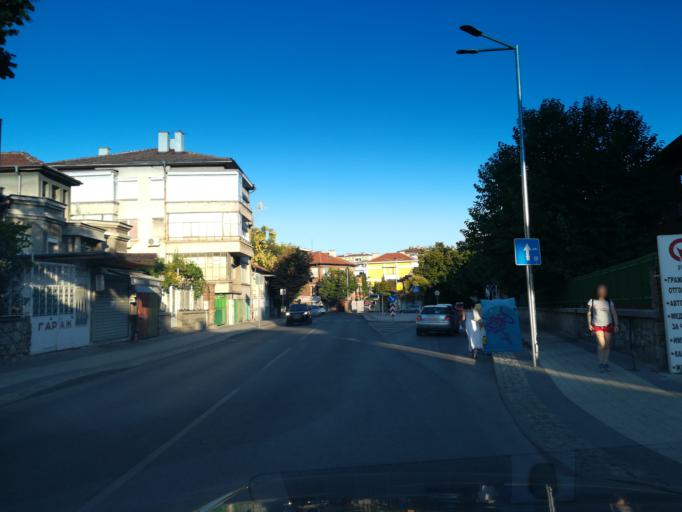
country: BG
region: Plovdiv
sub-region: Obshtina Plovdiv
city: Plovdiv
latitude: 42.1411
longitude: 24.7361
